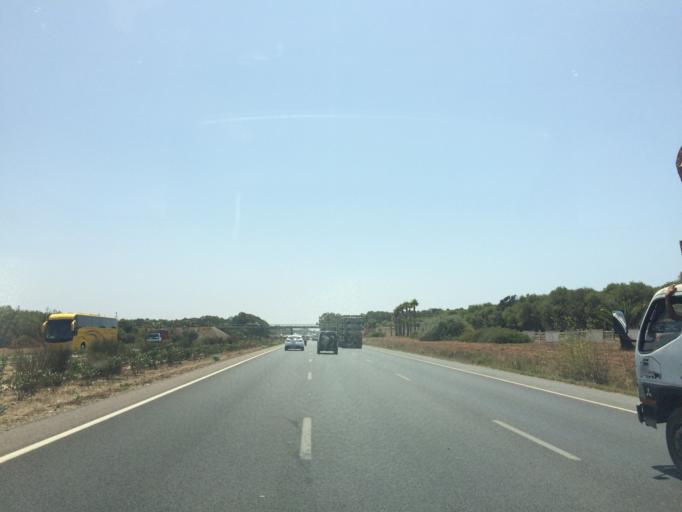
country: MA
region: Rabat-Sale-Zemmour-Zaer
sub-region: Skhirate-Temara
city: Temara
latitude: 33.9523
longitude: -6.9156
